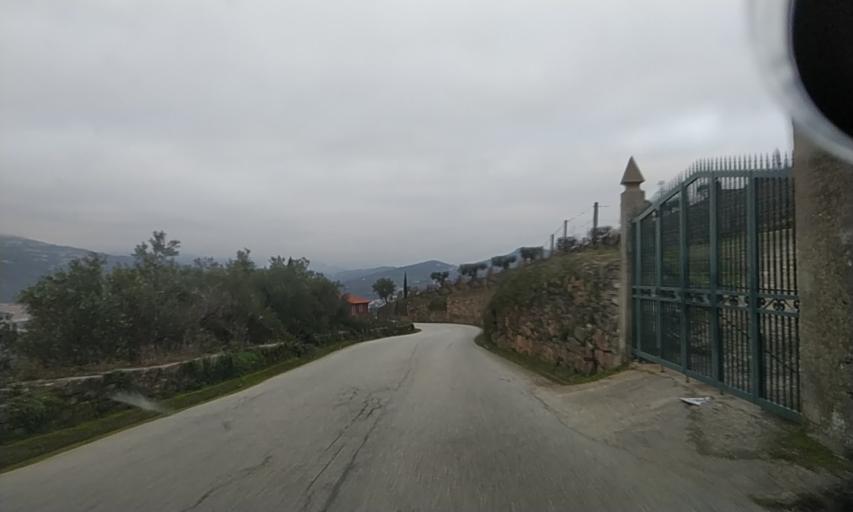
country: PT
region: Vila Real
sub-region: Peso da Regua
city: Peso da Regua
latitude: 41.1396
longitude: -7.7919
